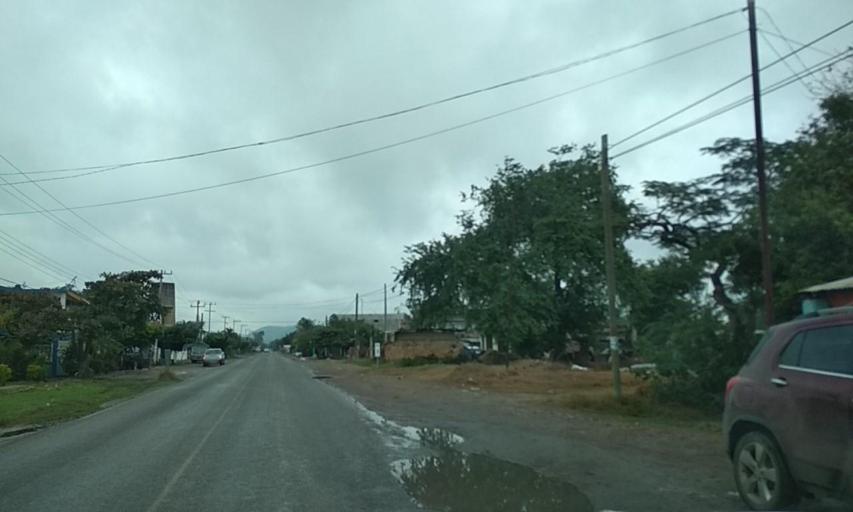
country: MX
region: Veracruz
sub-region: Papantla
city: El Chote
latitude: 20.3729
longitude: -97.3340
